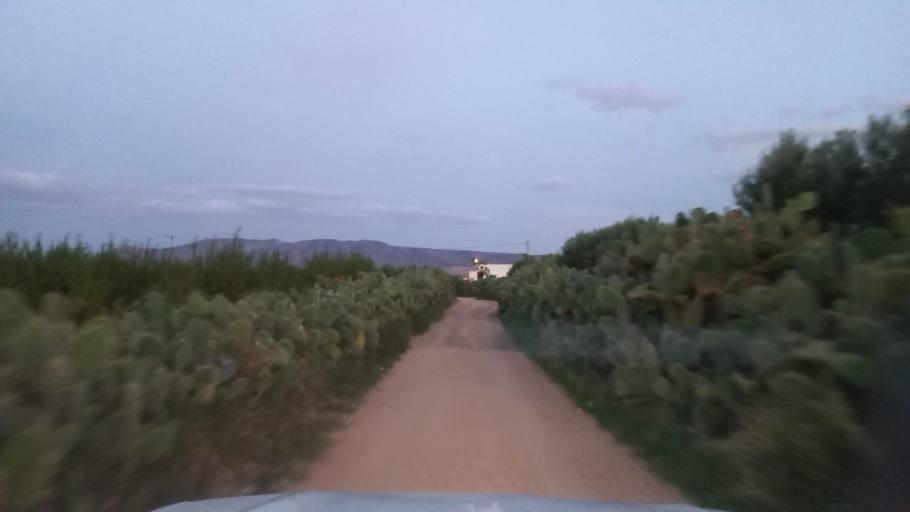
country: TN
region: Al Qasrayn
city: Sbiba
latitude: 35.4166
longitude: 9.1188
